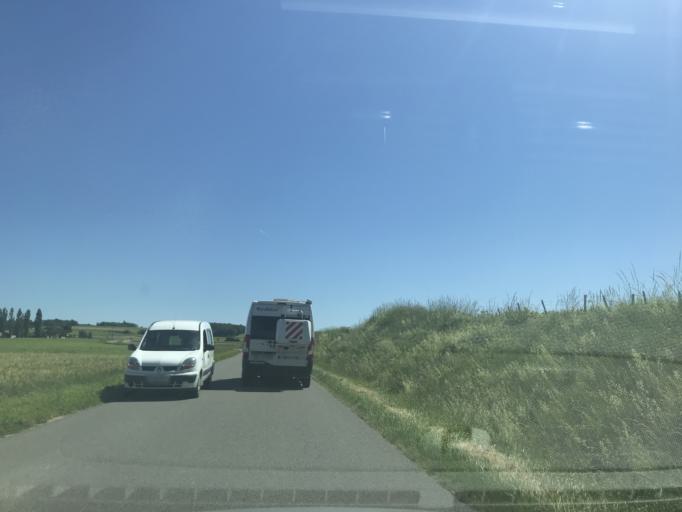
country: FR
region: Poitou-Charentes
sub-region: Departement de la Charente-Maritime
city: Mortagne-sur-Gironde
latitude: 45.4252
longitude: -0.7073
